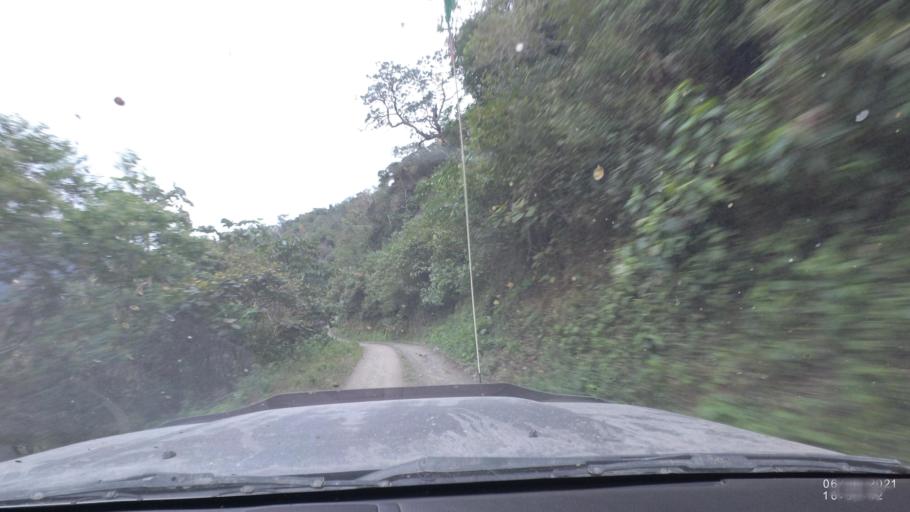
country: BO
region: La Paz
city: Quime
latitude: -16.5271
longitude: -66.7593
